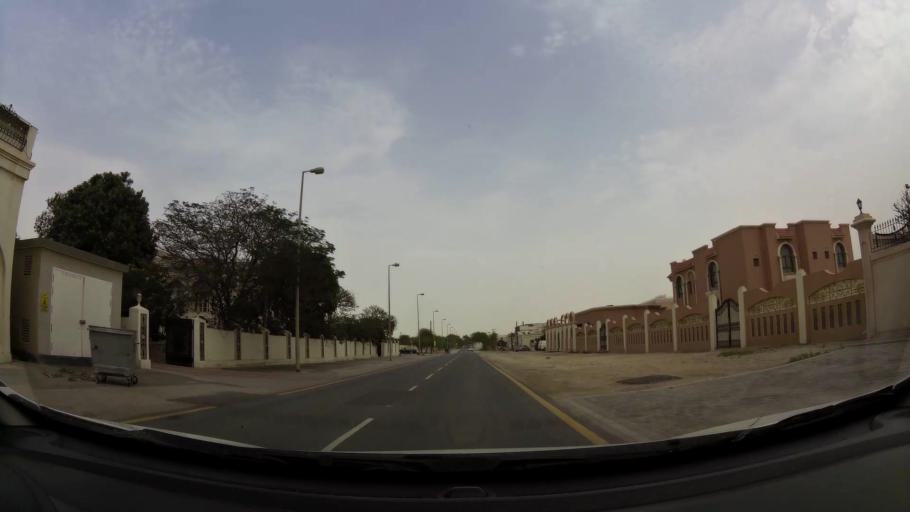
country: BH
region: Central Governorate
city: Madinat Hamad
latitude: 26.1198
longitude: 50.5308
